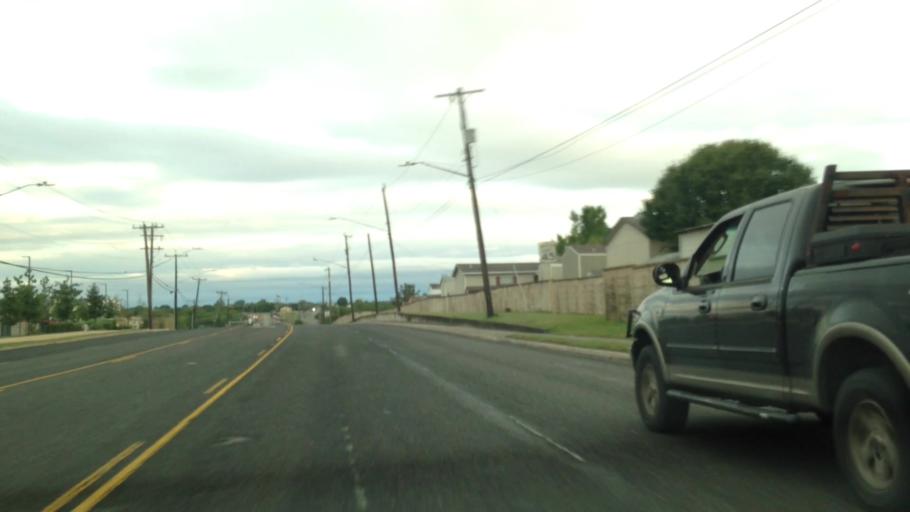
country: US
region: Texas
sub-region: Bexar County
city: Live Oak
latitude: 29.5618
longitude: -98.3616
